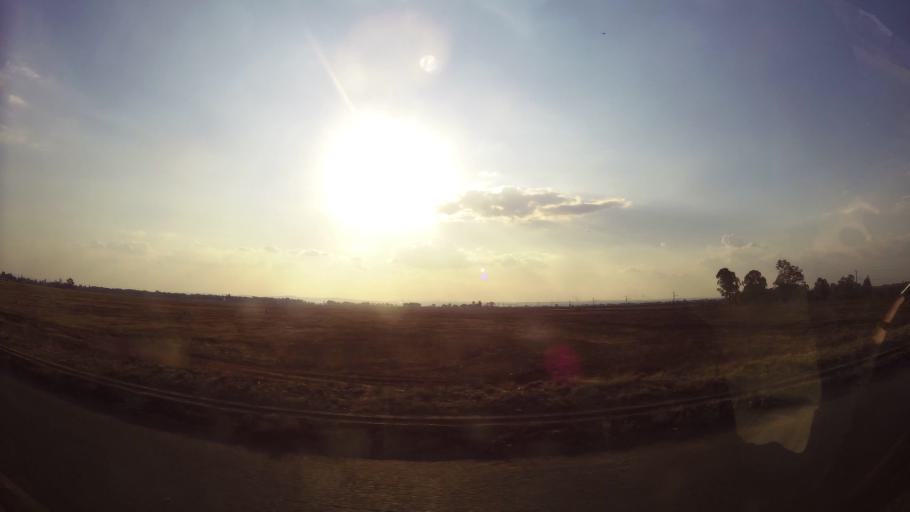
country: ZA
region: Gauteng
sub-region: Ekurhuleni Metropolitan Municipality
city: Germiston
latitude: -26.3299
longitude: 28.2365
